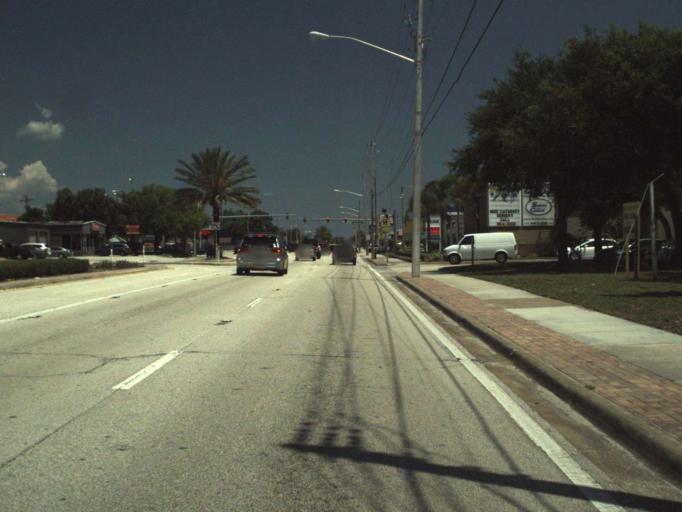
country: US
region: Florida
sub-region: Brevard County
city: Rockledge
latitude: 28.3598
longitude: -80.7001
